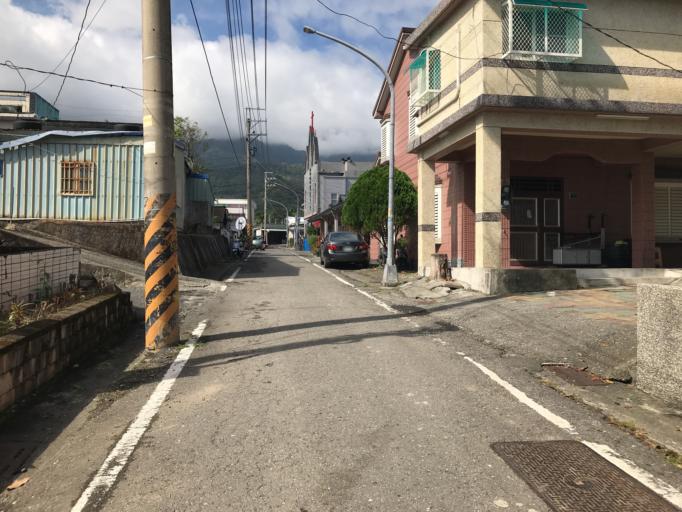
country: TW
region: Taiwan
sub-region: Taitung
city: Taitung
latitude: 23.1922
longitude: 121.3956
